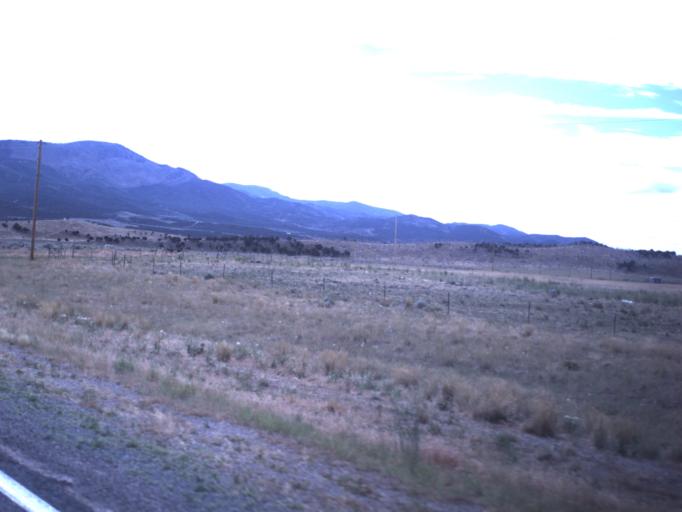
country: US
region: Utah
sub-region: Beaver County
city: Beaver
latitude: 38.6108
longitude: -112.6004
